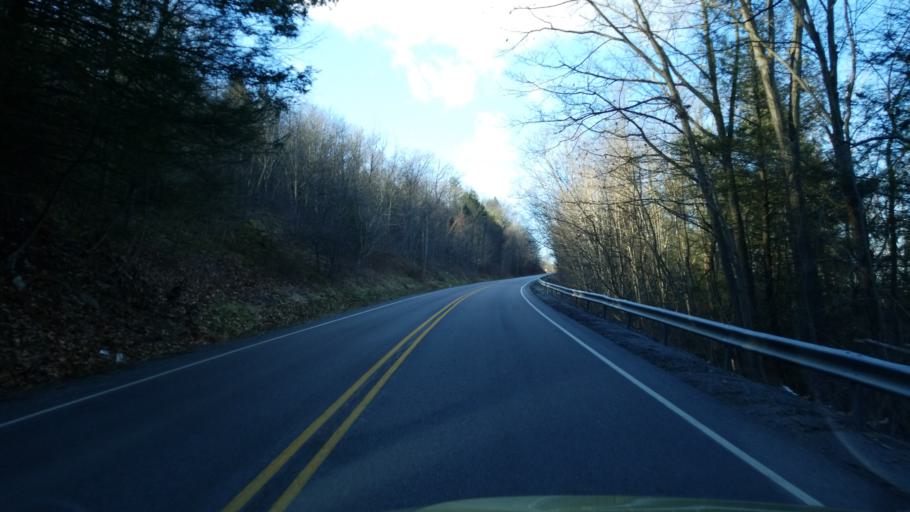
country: US
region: Pennsylvania
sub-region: Clearfield County
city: Clearfield
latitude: 41.0009
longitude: -78.4323
